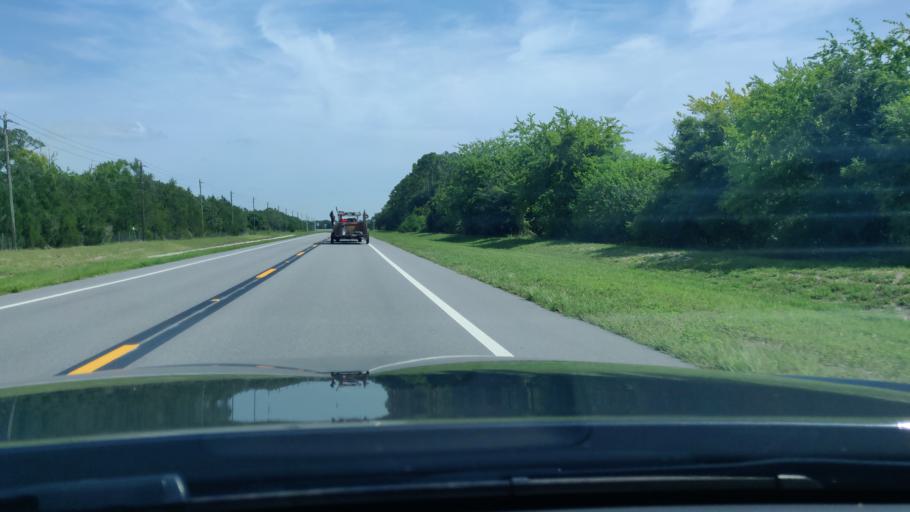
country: US
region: Florida
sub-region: Flagler County
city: Flagler Beach
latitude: 29.5106
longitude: -81.1620
